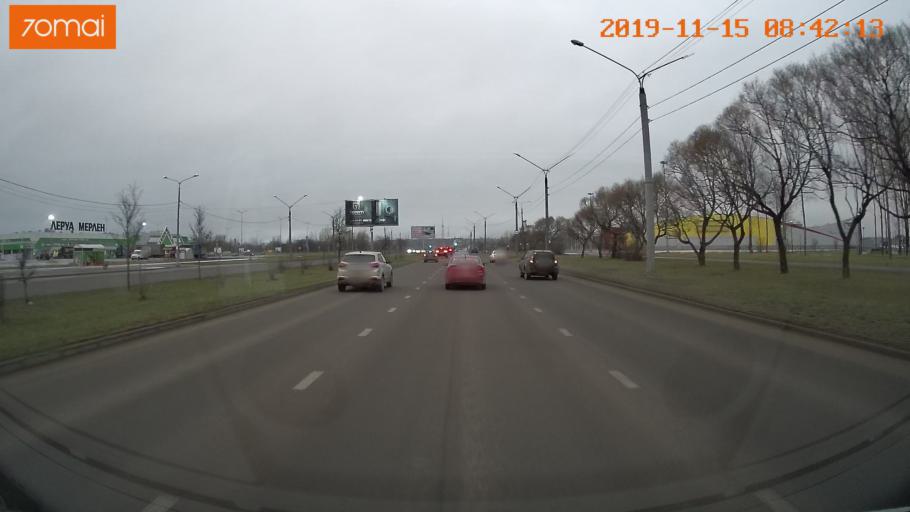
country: RU
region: Vologda
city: Cherepovets
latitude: 59.1014
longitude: 37.9091
